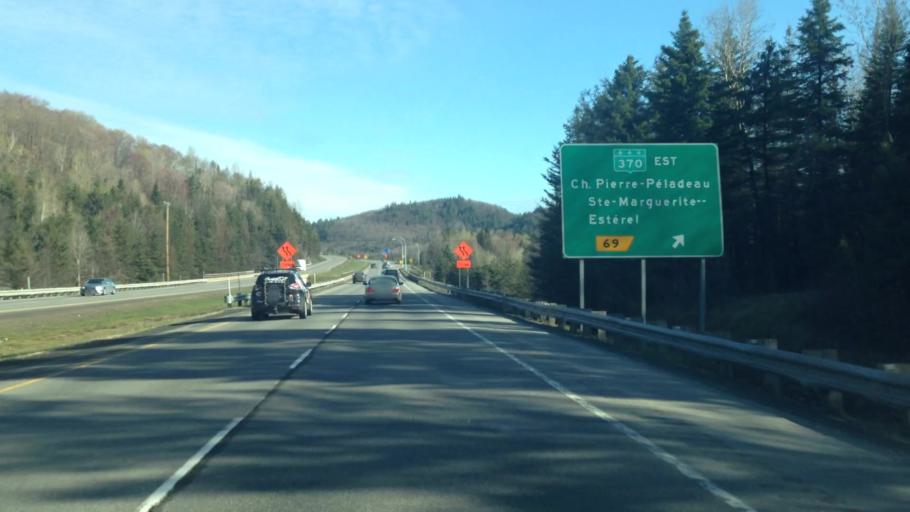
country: CA
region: Quebec
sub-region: Laurentides
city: Sainte-Adele
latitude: 45.9513
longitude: -74.1262
